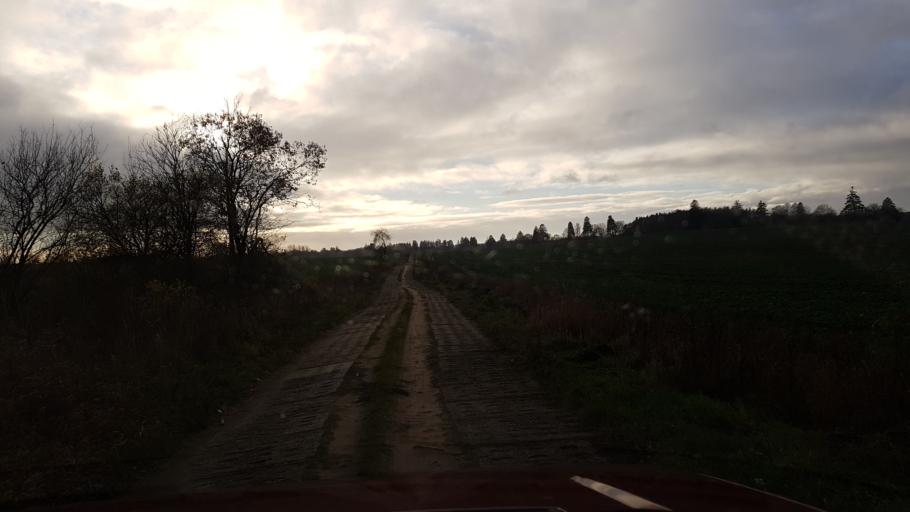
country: PL
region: West Pomeranian Voivodeship
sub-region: Powiat szczecinecki
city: Grzmiaca
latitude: 53.9901
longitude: 16.4090
